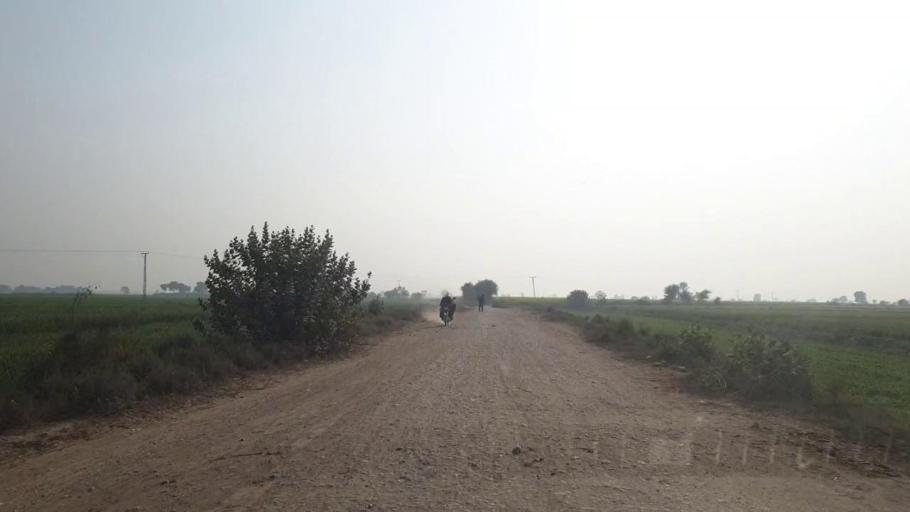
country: PK
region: Sindh
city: Hala
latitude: 25.7602
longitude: 68.3840
